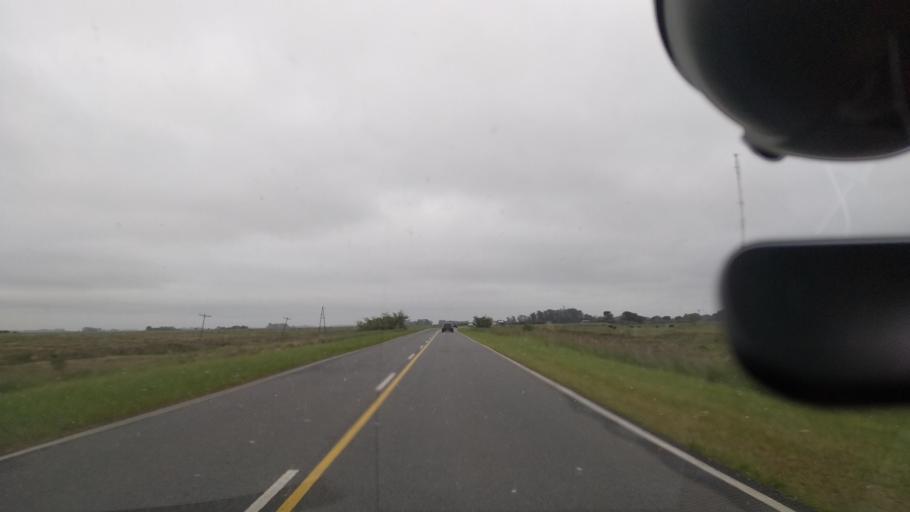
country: AR
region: Buenos Aires
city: Veronica
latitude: -35.4433
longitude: -57.3410
